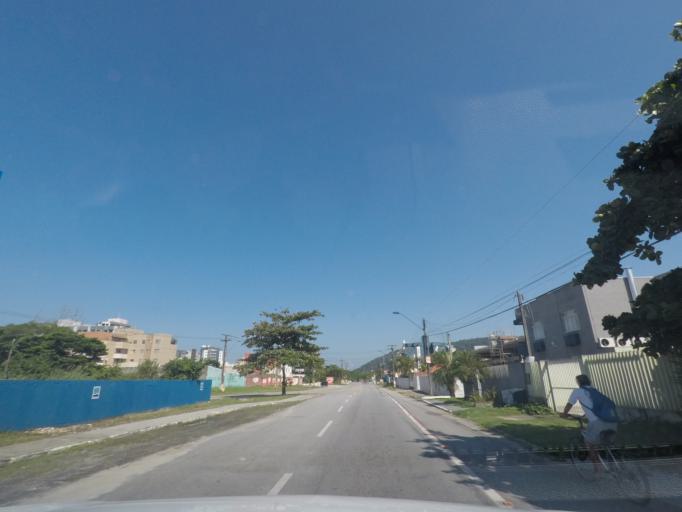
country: BR
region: Parana
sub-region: Guaratuba
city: Guaratuba
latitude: -25.8305
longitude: -48.5391
